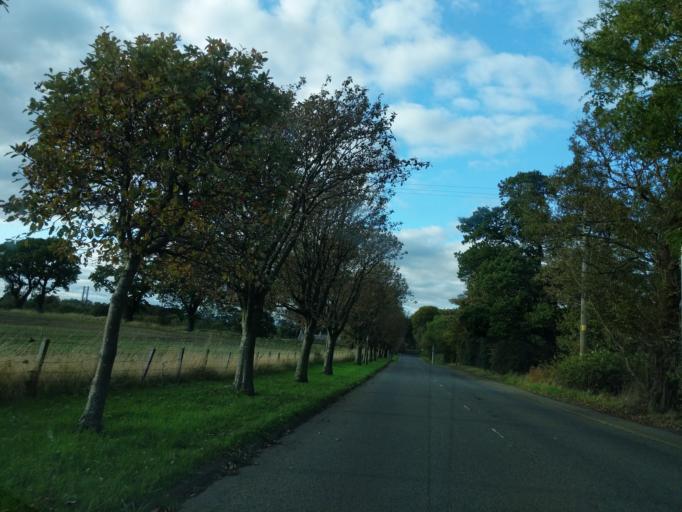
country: GB
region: Scotland
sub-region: Edinburgh
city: Queensferry
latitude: 55.9846
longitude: -3.3750
